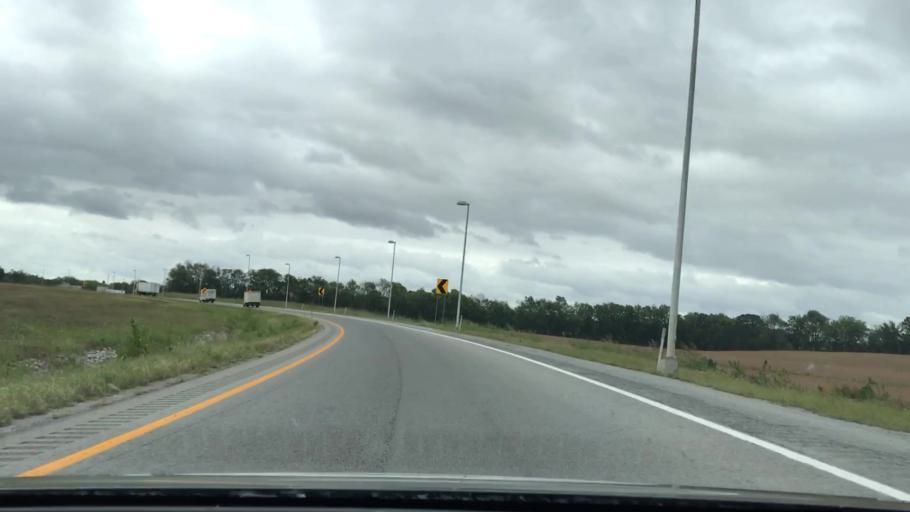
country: US
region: Kentucky
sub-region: Christian County
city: Fort Campbell North
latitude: 36.7385
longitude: -87.5075
